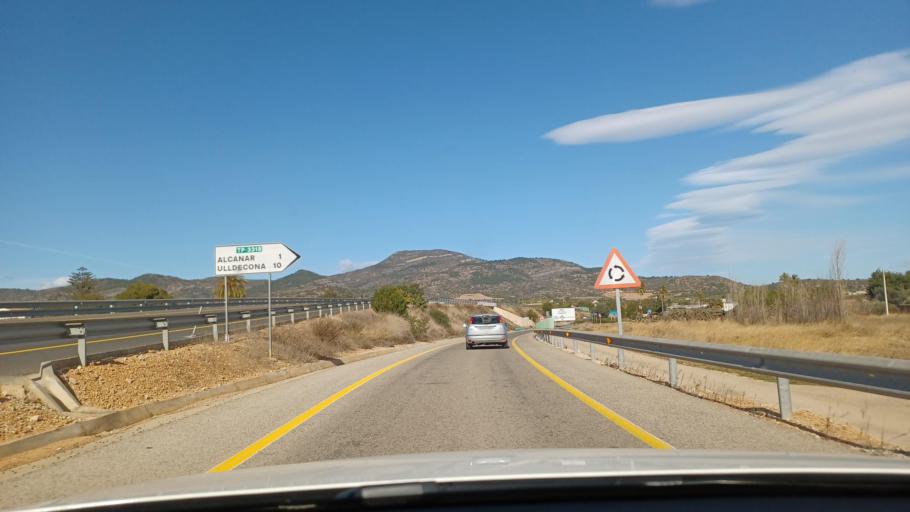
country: ES
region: Catalonia
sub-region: Provincia de Tarragona
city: Alcanar
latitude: 40.5461
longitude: 0.5085
